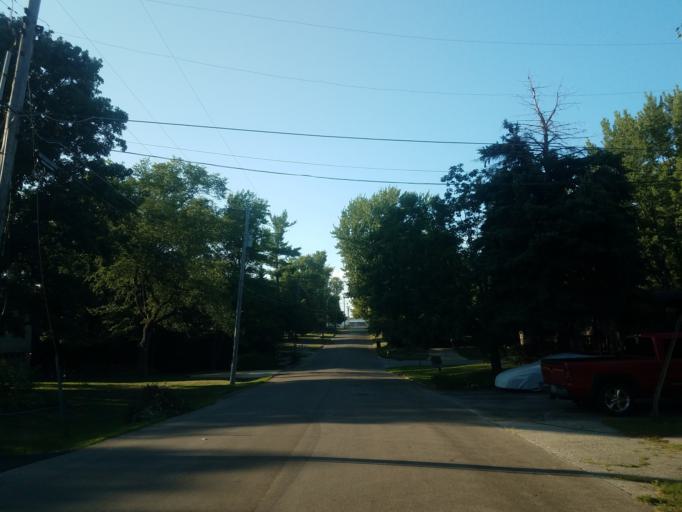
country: US
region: Illinois
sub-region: McLean County
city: Bloomington
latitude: 40.4643
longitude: -88.9769
